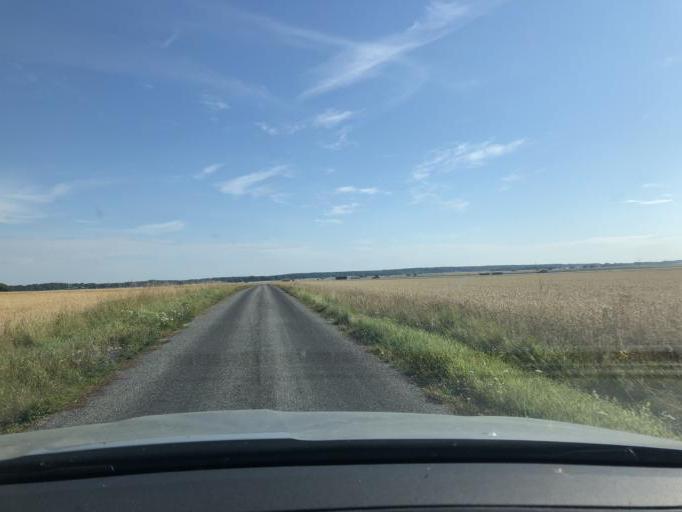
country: SE
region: Uppsala
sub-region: Enkopings Kommun
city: Irsta
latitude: 59.7436
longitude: 16.9446
